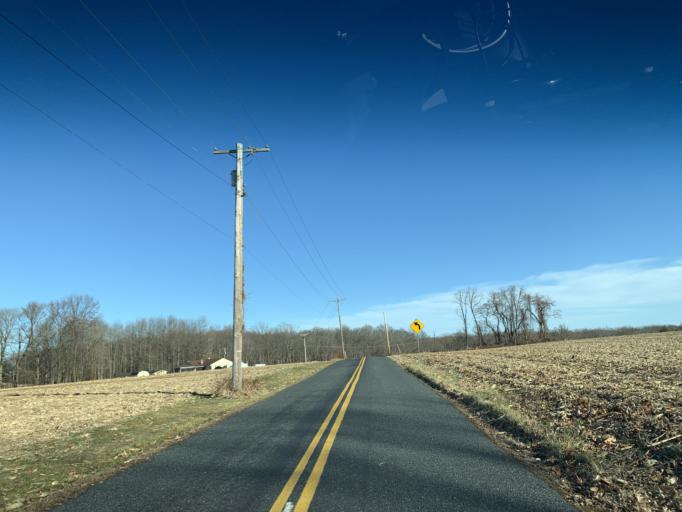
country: US
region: Maryland
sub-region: Harford County
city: Riverside
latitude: 39.5355
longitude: -76.2420
